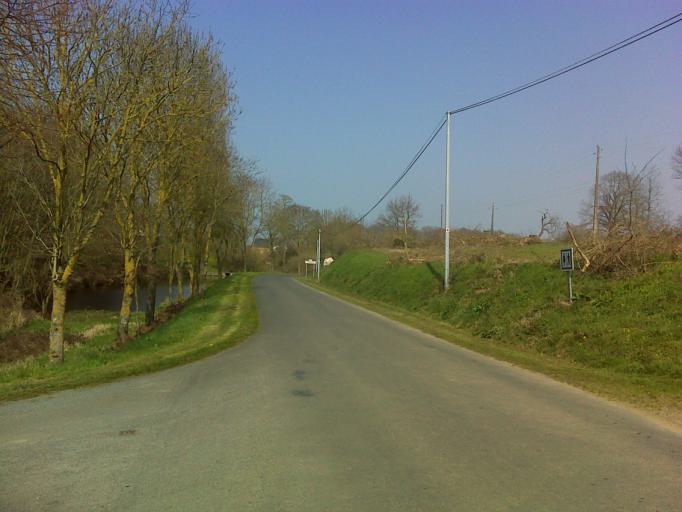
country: FR
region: Brittany
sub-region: Departement d'Ille-et-Vilaine
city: Saint-Broladre
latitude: 48.5860
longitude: -1.6353
